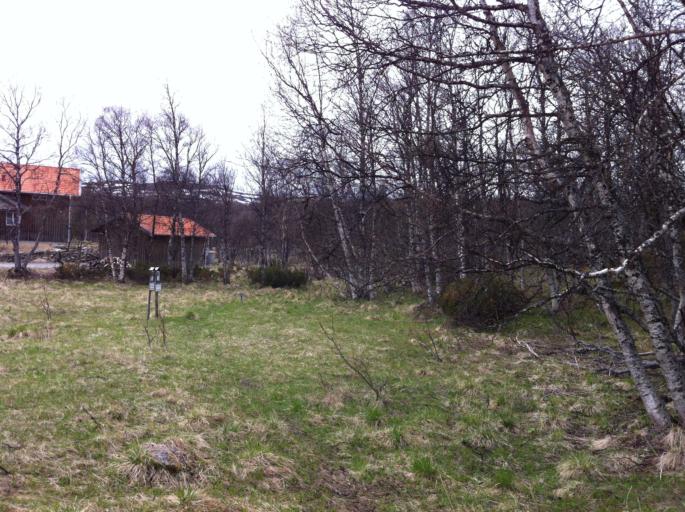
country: NO
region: Sor-Trondelag
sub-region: Tydal
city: Aas
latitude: 62.5531
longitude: 12.3147
